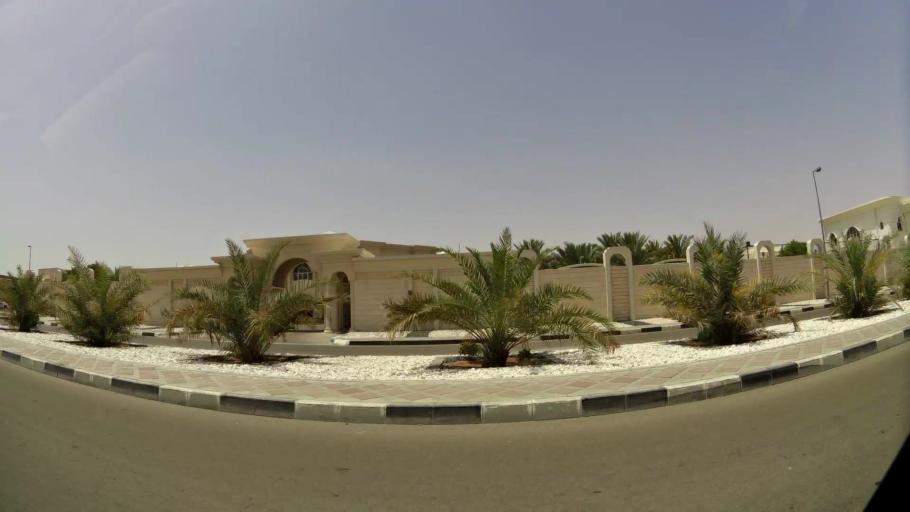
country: AE
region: Abu Dhabi
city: Al Ain
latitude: 24.1996
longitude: 55.7404
